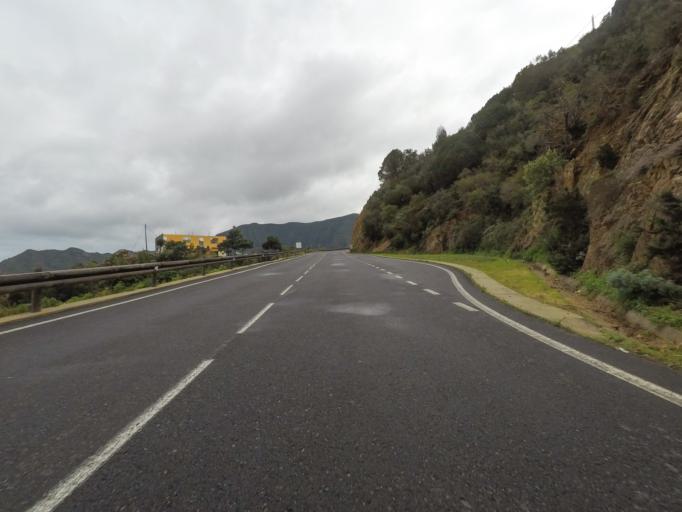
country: ES
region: Canary Islands
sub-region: Provincia de Santa Cruz de Tenerife
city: Vallehermosa
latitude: 28.1692
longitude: -17.2784
